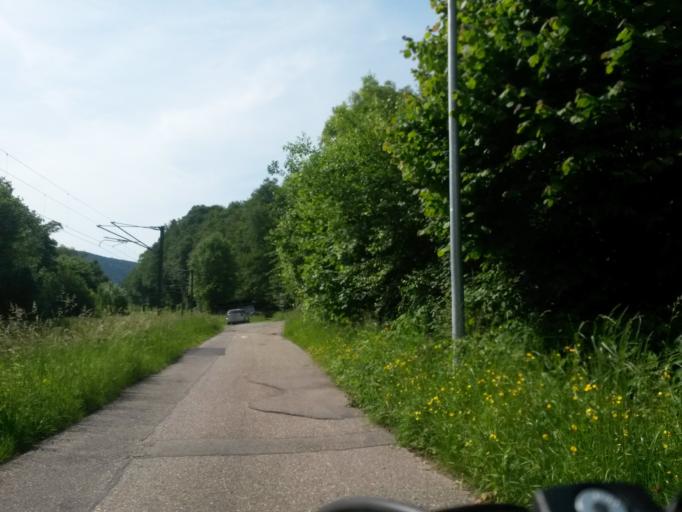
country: DE
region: Baden-Wuerttemberg
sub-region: Karlsruhe Region
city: Hofen an der Enz
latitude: 48.8245
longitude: 8.5753
